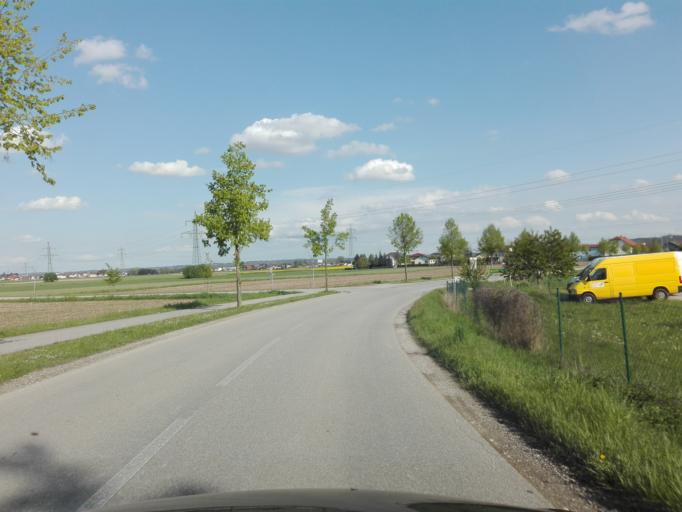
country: AT
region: Upper Austria
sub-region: Politischer Bezirk Linz-Land
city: Horsching
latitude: 48.2123
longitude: 14.1834
